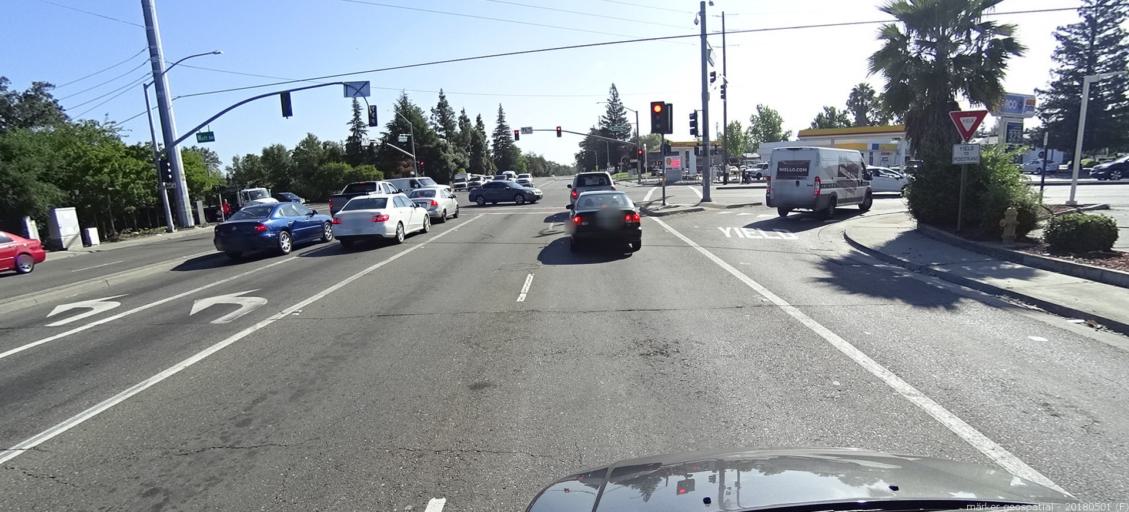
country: US
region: California
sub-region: Sacramento County
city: Arden-Arcade
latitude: 38.6369
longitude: -121.3835
